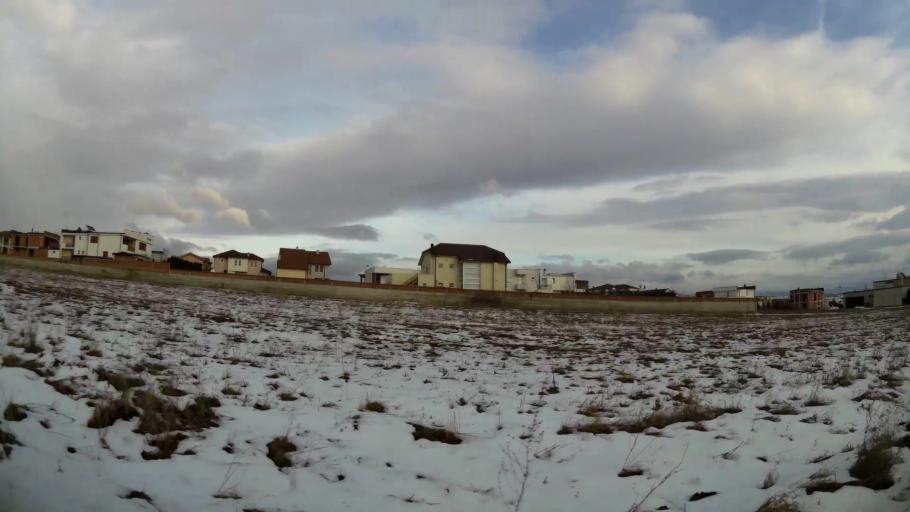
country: XK
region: Pristina
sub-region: Komuna e Prishtines
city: Pristina
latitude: 42.6235
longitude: 21.1587
